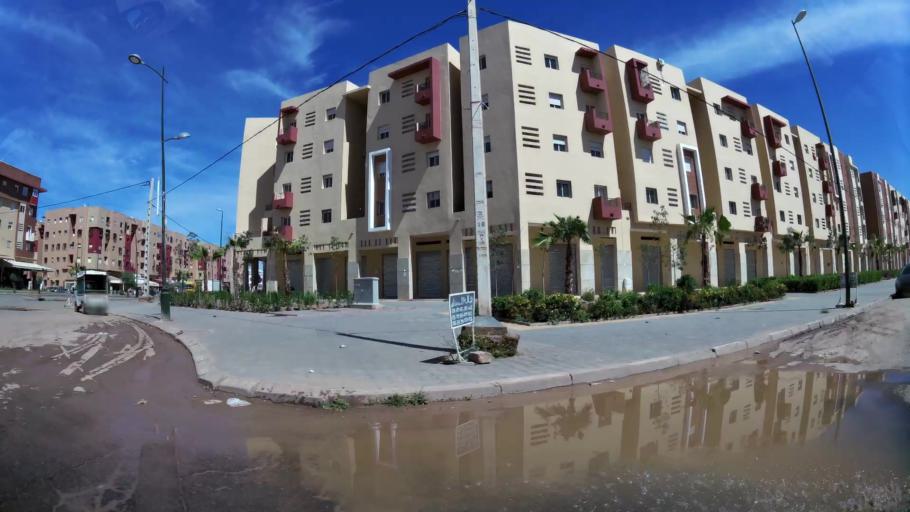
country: MA
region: Marrakech-Tensift-Al Haouz
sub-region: Marrakech
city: Marrakesh
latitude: 31.6395
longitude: -8.0751
